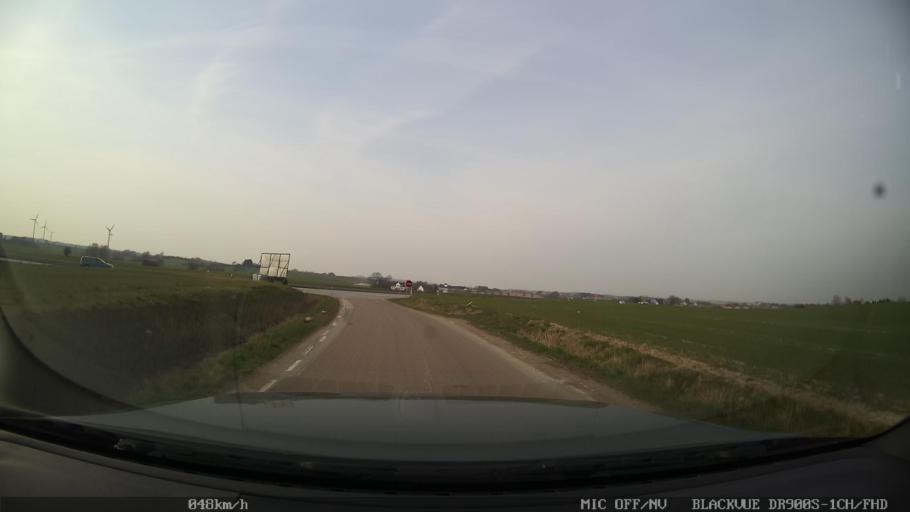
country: SE
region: Skane
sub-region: Ystads Kommun
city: Ystad
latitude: 55.4754
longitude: 13.8003
